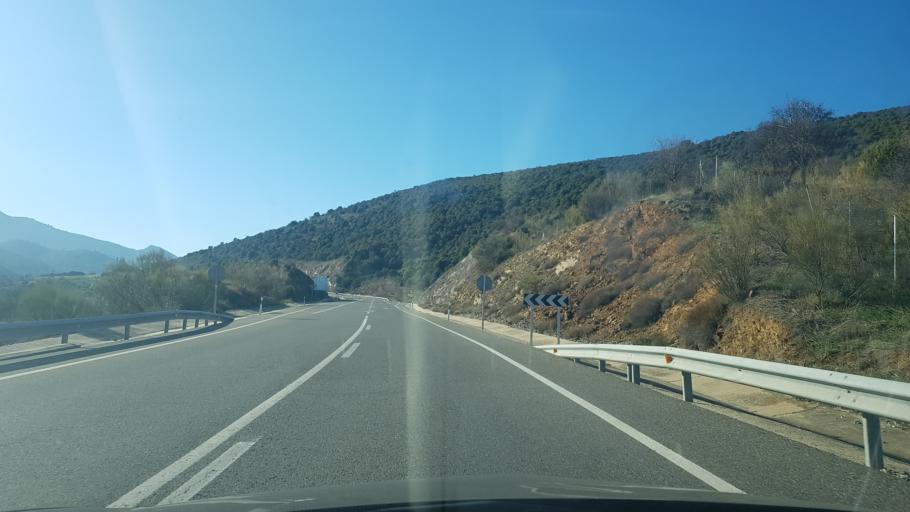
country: ES
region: Castille and Leon
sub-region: Provincia de Avila
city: El Tiemblo
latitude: 40.4306
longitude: -4.5198
